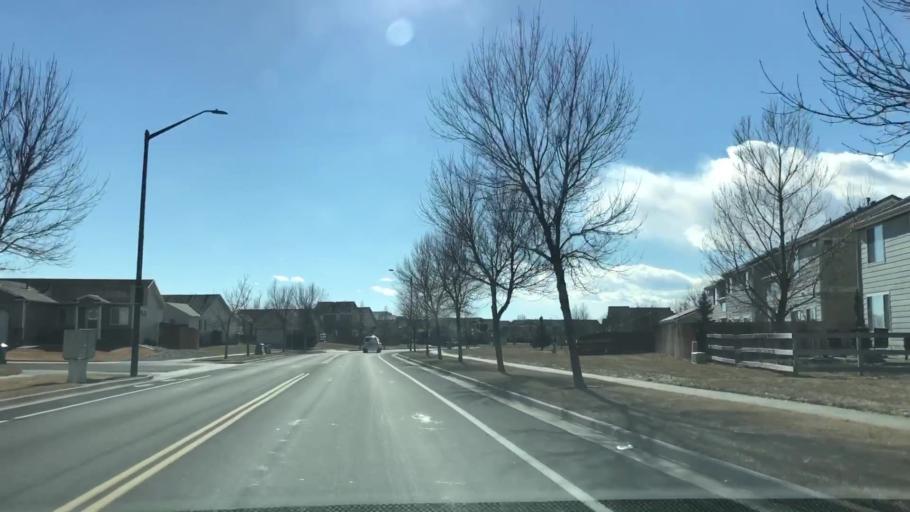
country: US
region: Colorado
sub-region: Larimer County
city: Fort Collins
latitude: 40.5998
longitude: -105.0037
